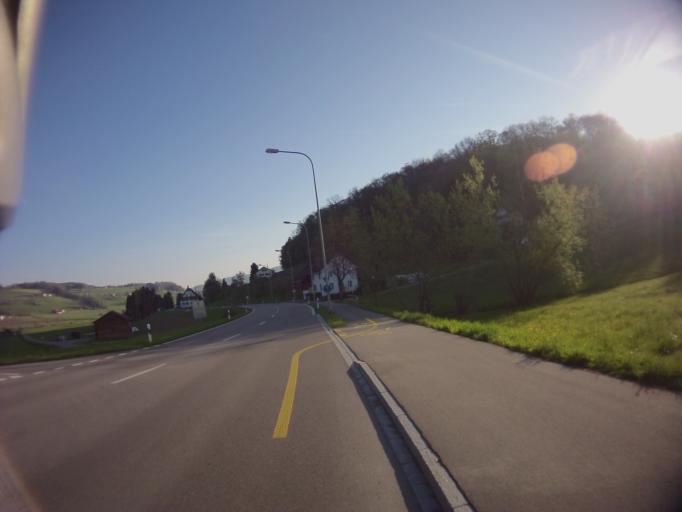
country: CH
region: Zurich
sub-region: Bezirk Affoltern
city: Hedingen
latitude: 47.3031
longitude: 8.4490
